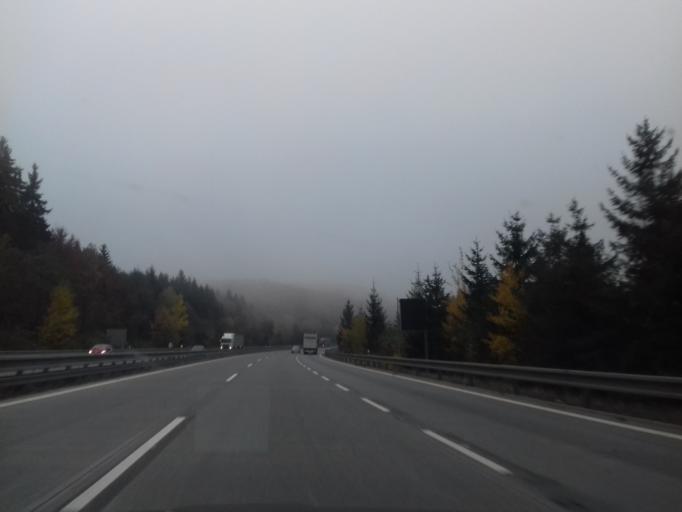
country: CZ
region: Vysocina
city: Stoky
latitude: 49.4676
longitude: 15.5728
